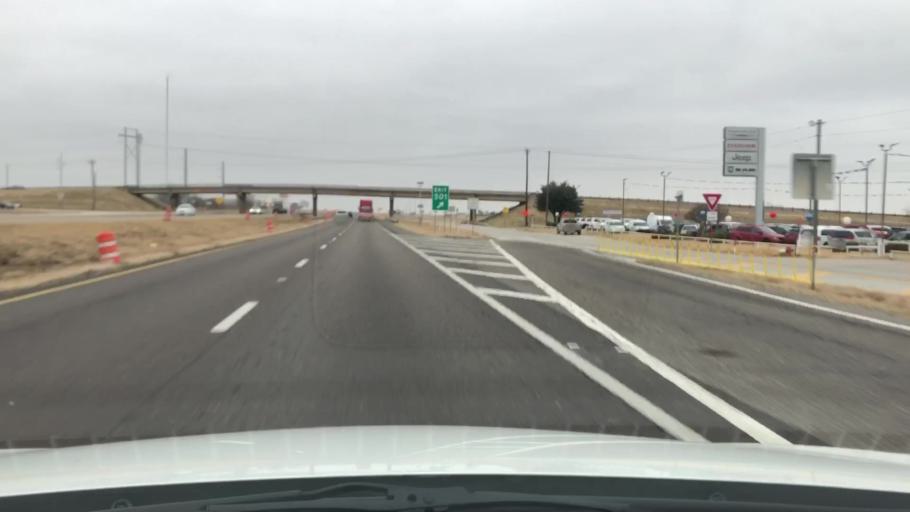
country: US
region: Texas
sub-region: Cooke County
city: Gainesville
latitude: 33.6799
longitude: -97.1552
